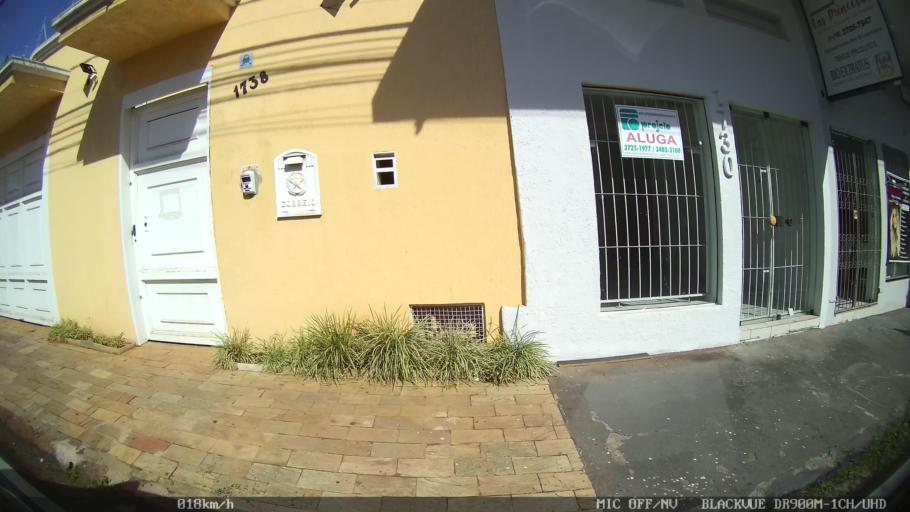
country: BR
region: Sao Paulo
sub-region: Franca
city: Franca
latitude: -20.5362
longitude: -47.3984
